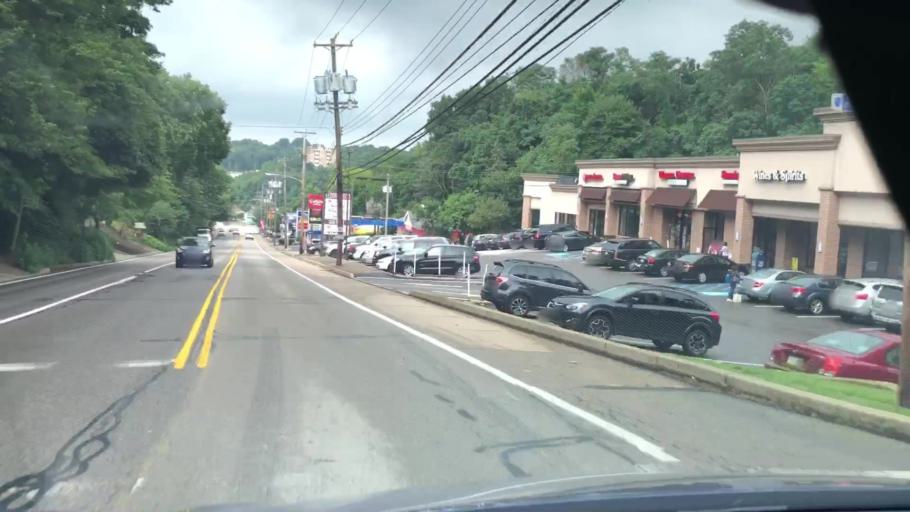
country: US
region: Pennsylvania
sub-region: Allegheny County
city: Green Tree
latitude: 40.3910
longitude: -80.0594
